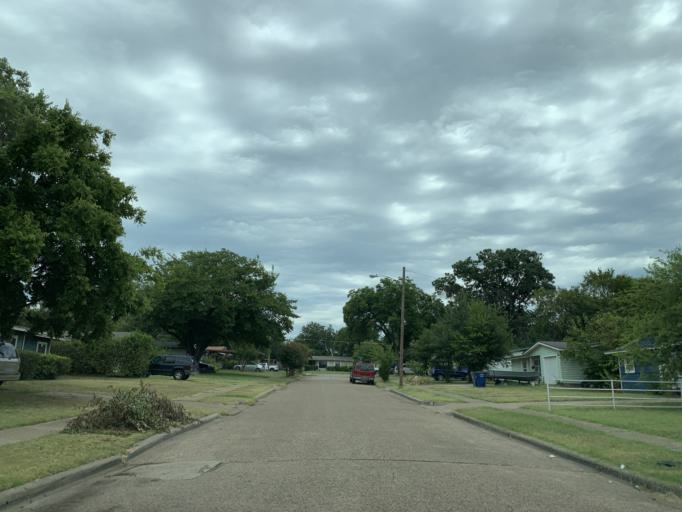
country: US
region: Texas
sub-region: Dallas County
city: DeSoto
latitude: 32.6599
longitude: -96.8330
